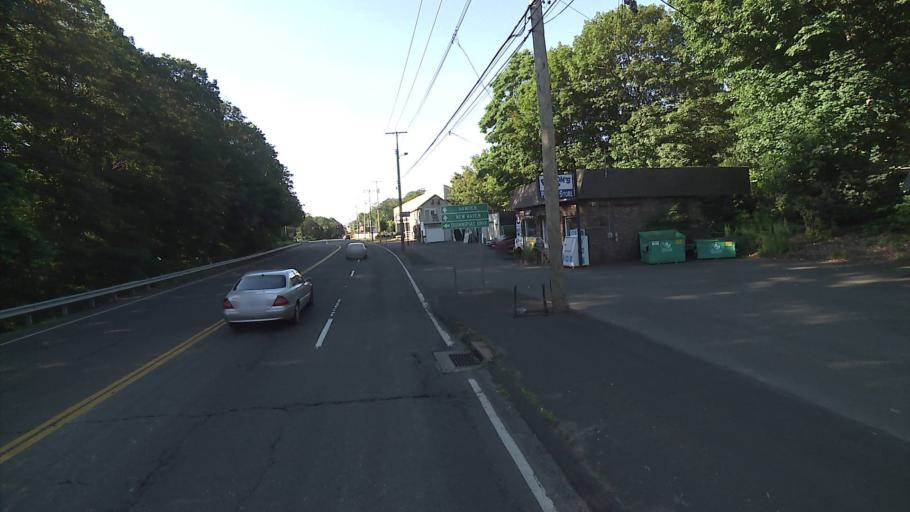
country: US
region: Connecticut
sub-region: New Haven County
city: Hamden
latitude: 41.4226
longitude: -72.9054
